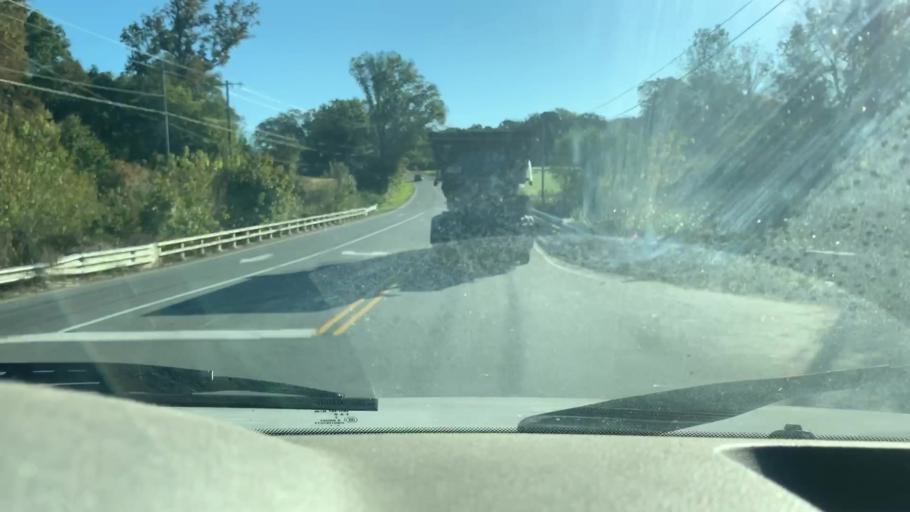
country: US
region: North Carolina
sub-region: Cabarrus County
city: Harrisburg
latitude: 35.4082
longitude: -80.7306
